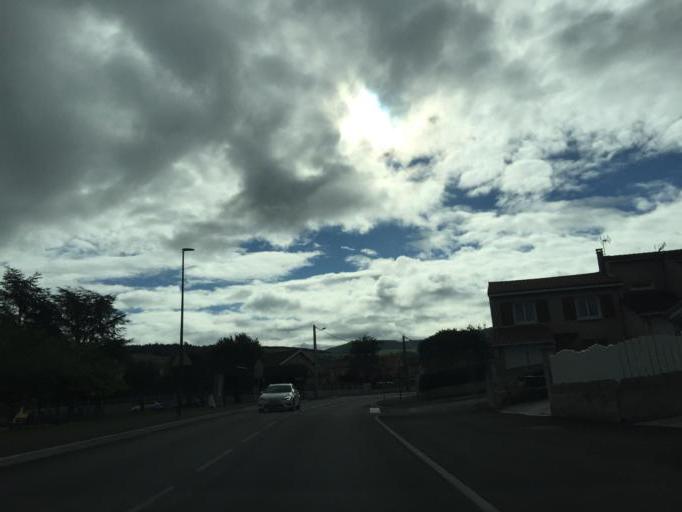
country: FR
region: Rhone-Alpes
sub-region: Departement de la Loire
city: Saint-Paul-en-Jarez
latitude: 45.4854
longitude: 4.5750
